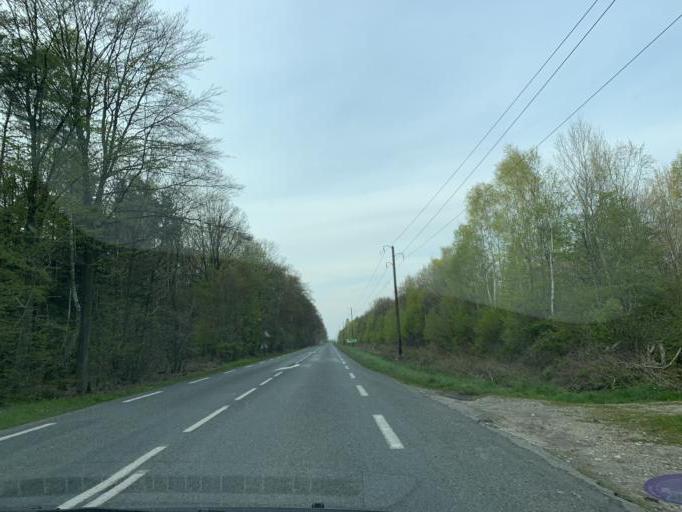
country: FR
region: Haute-Normandie
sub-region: Departement de la Seine-Maritime
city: Jumieges
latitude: 49.4188
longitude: 0.7953
